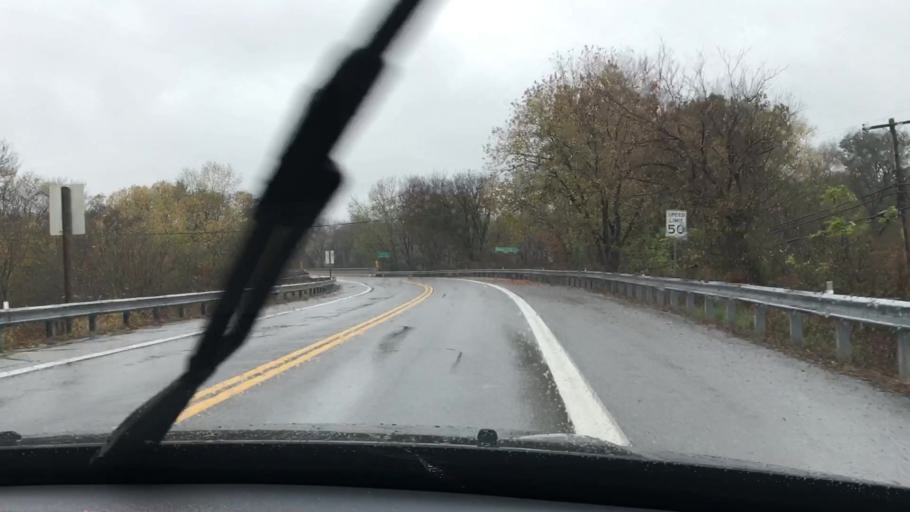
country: US
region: Maryland
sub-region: Frederick County
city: Buckeystown
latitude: 39.3267
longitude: -77.4118
